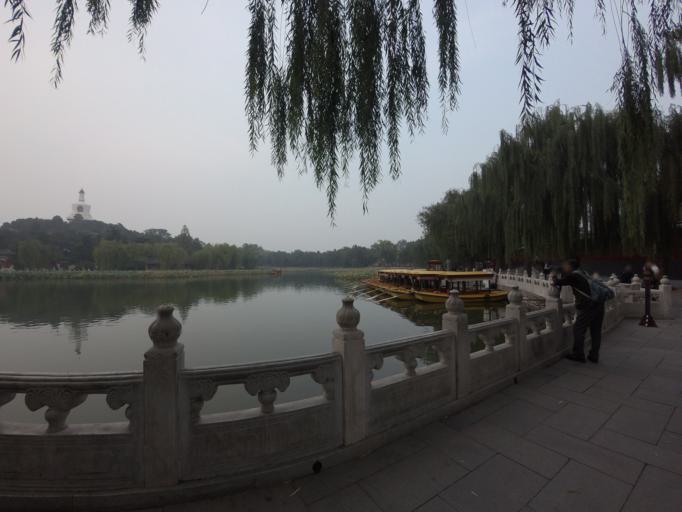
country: CN
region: Beijing
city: Beijing
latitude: 39.9217
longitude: 116.3836
